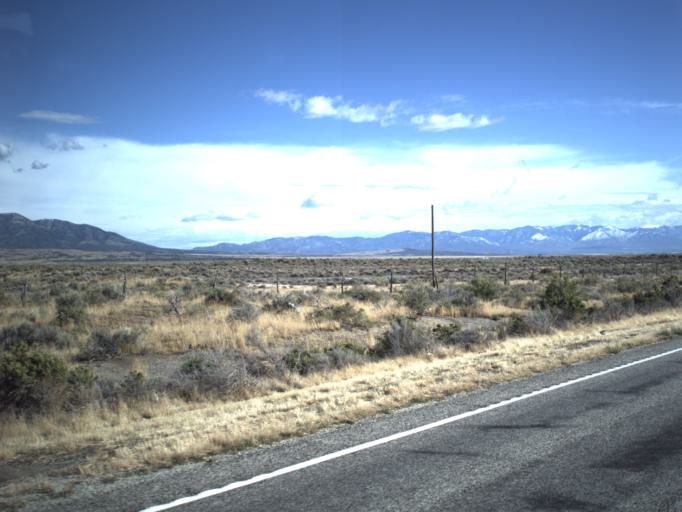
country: US
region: Utah
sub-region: Millard County
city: Delta
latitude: 39.3065
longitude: -112.4748
